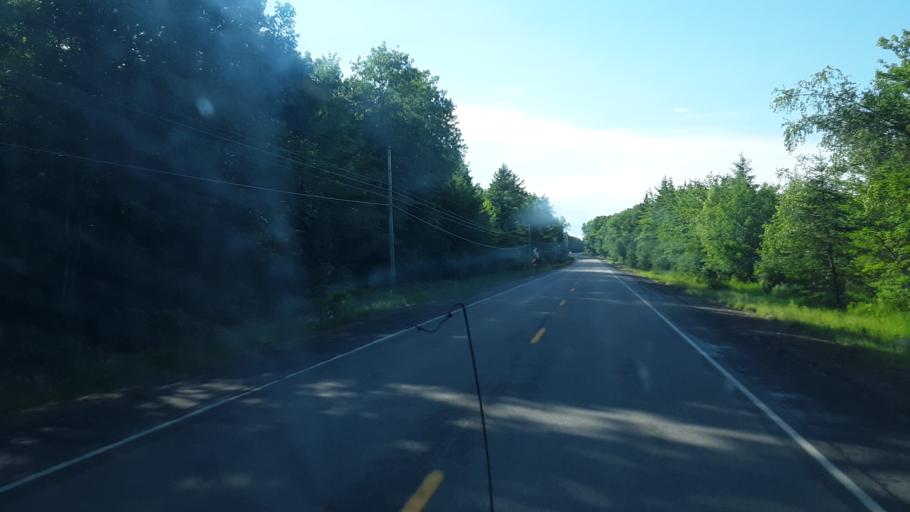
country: US
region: Maine
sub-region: Washington County
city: Calais
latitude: 45.3530
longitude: -67.7034
